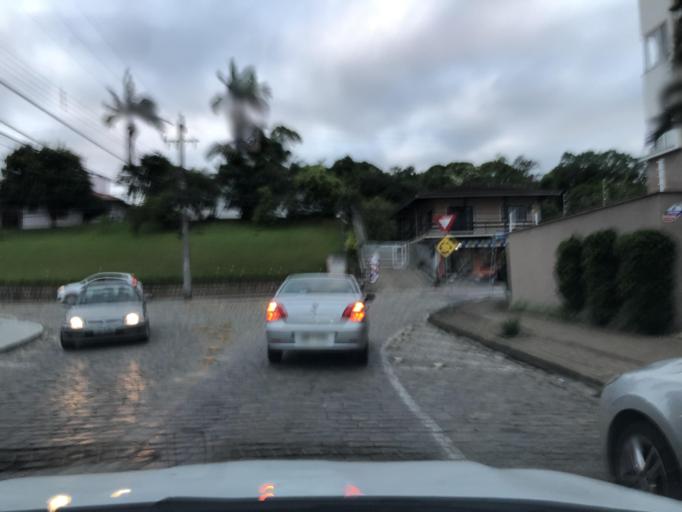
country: BR
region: Santa Catarina
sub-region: Joinville
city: Joinville
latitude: -26.2906
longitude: -48.8725
